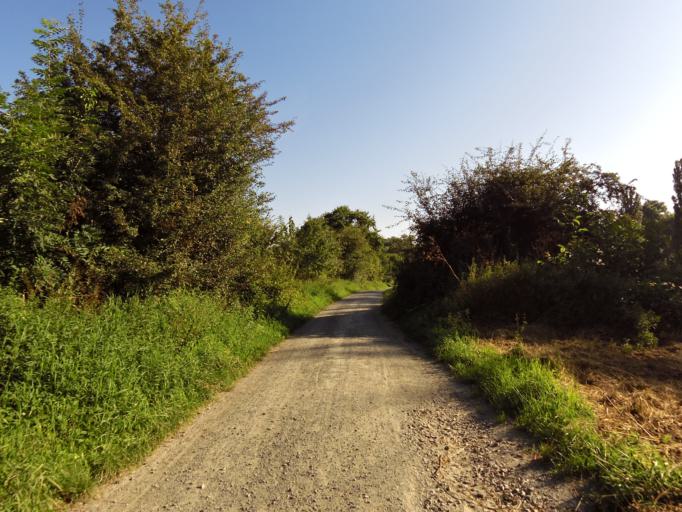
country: DE
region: Hesse
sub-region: Regierungsbezirk Darmstadt
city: Gross-Rohrheim
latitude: 49.7317
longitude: 8.4504
